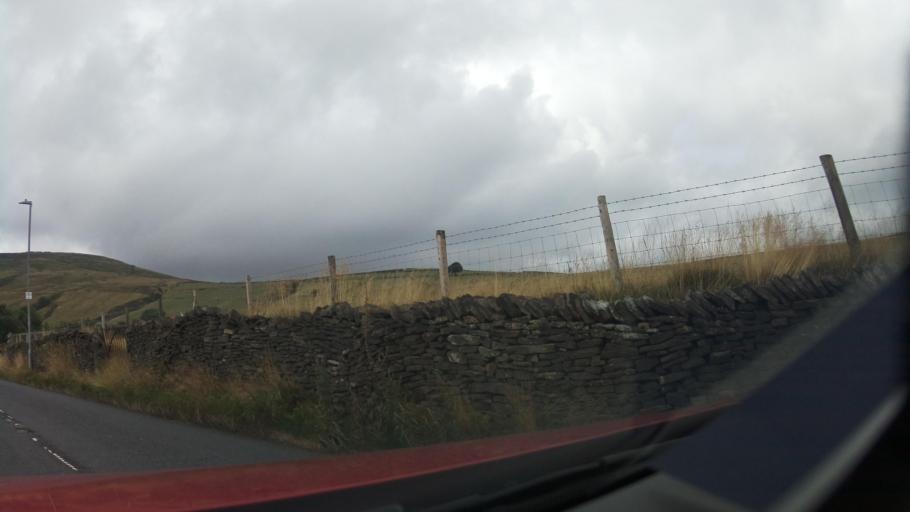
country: GB
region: England
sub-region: Kirklees
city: Meltham
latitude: 53.5479
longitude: -1.8413
